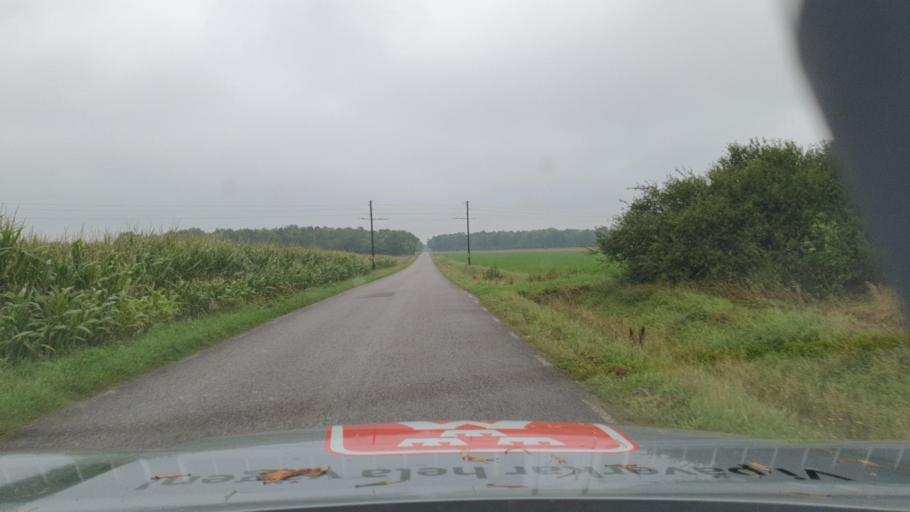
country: SE
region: Gotland
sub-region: Gotland
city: Visby
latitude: 57.7896
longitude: 18.5260
